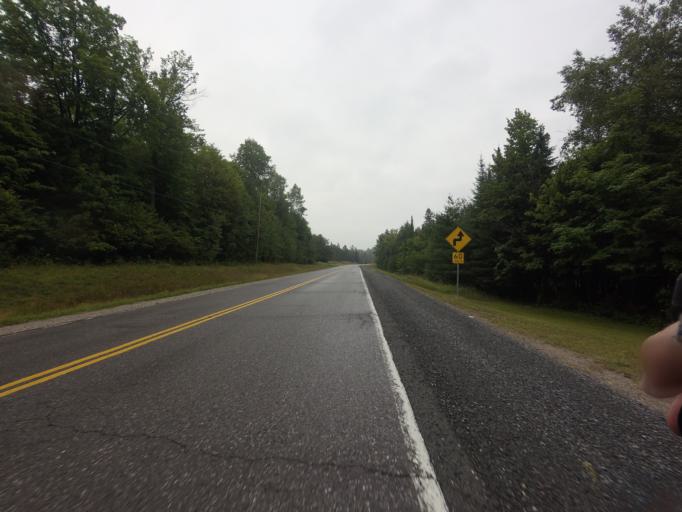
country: CA
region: Ontario
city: Carleton Place
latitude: 45.1191
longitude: -76.3506
